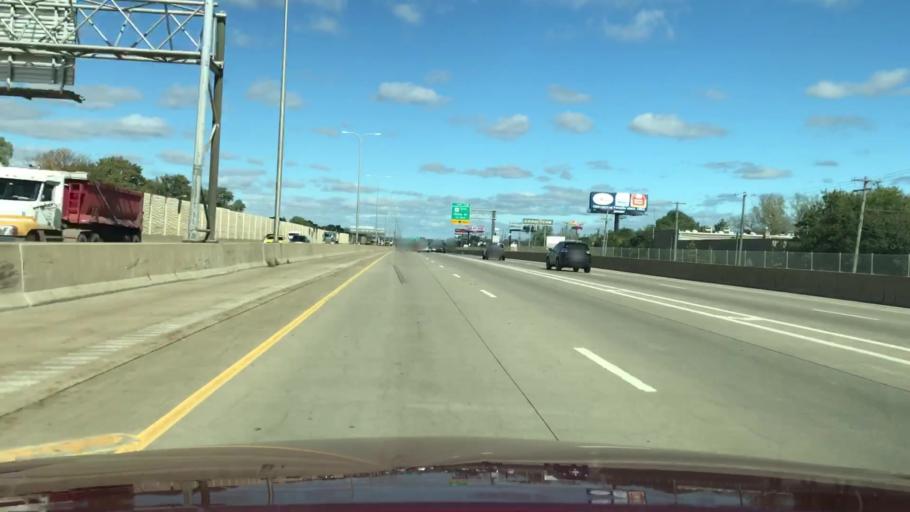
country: US
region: Illinois
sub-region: Cook County
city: South Holland
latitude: 41.5890
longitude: -87.5835
